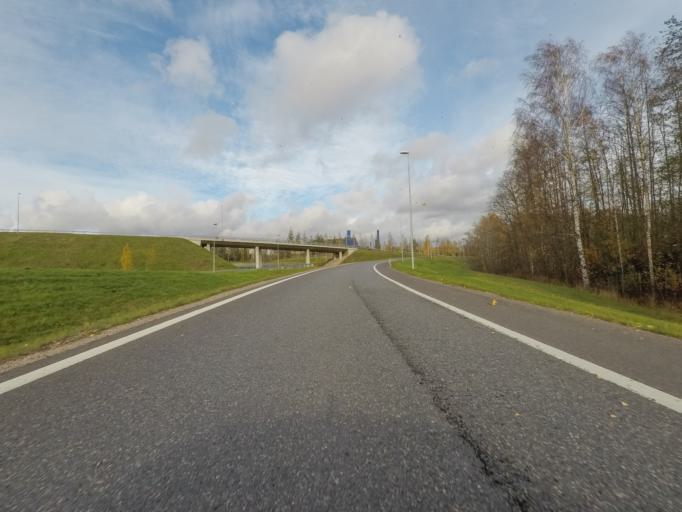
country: FI
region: Uusimaa
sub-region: Helsinki
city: Vantaa
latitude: 60.2561
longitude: 25.1290
